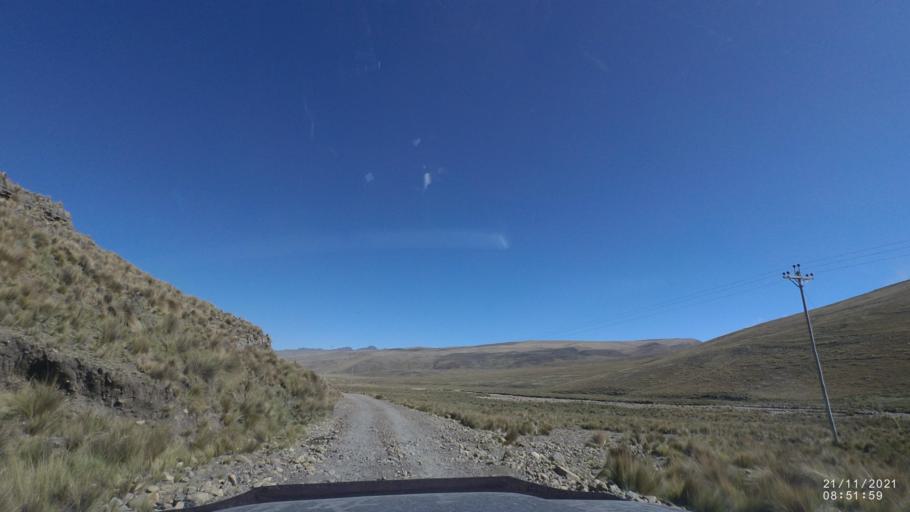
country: BO
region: Cochabamba
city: Cochabamba
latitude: -17.2159
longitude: -66.2378
